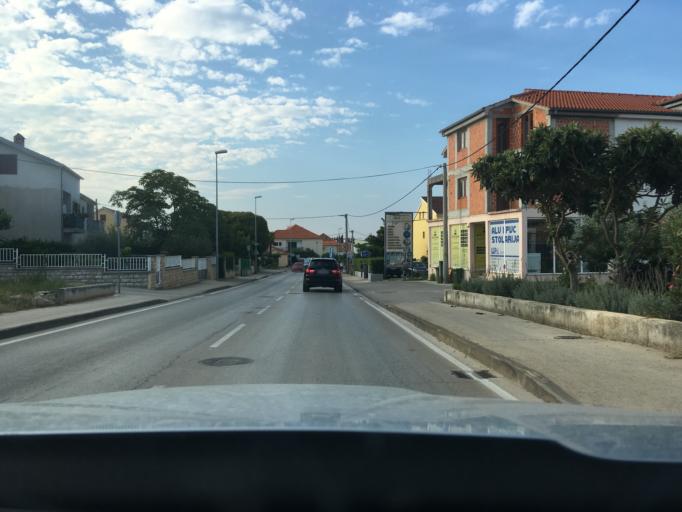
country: HR
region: Zadarska
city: Zadar
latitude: 44.1348
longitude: 15.2300
